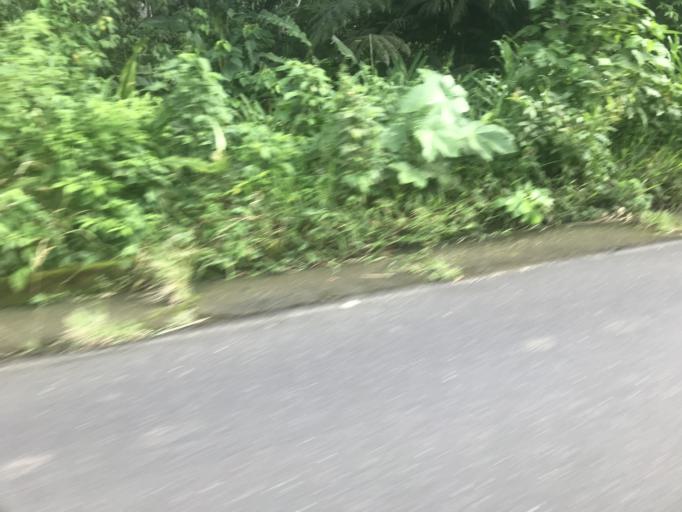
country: EC
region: Napo
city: Tena
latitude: -1.0424
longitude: -77.7997
